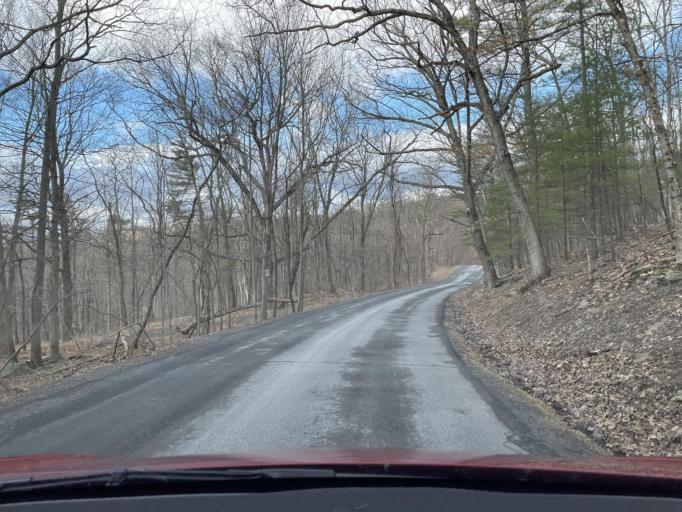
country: US
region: New York
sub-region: Ulster County
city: Woodstock
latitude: 42.0539
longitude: -74.1438
